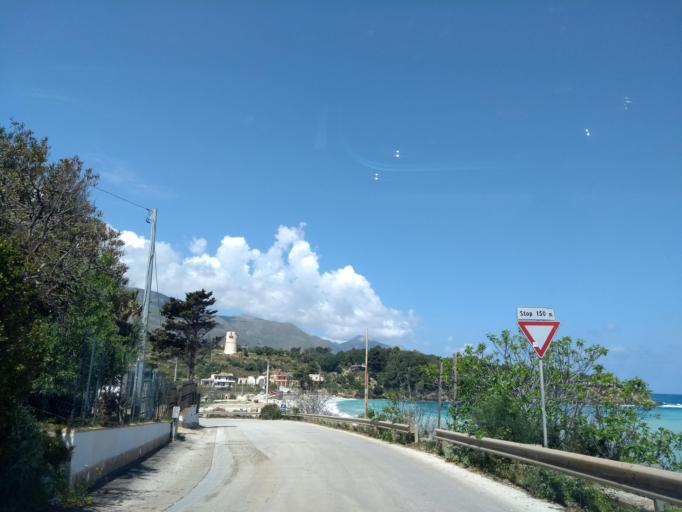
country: IT
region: Sicily
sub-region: Trapani
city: Castellammare del Golfo
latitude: 38.0556
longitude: 12.8415
